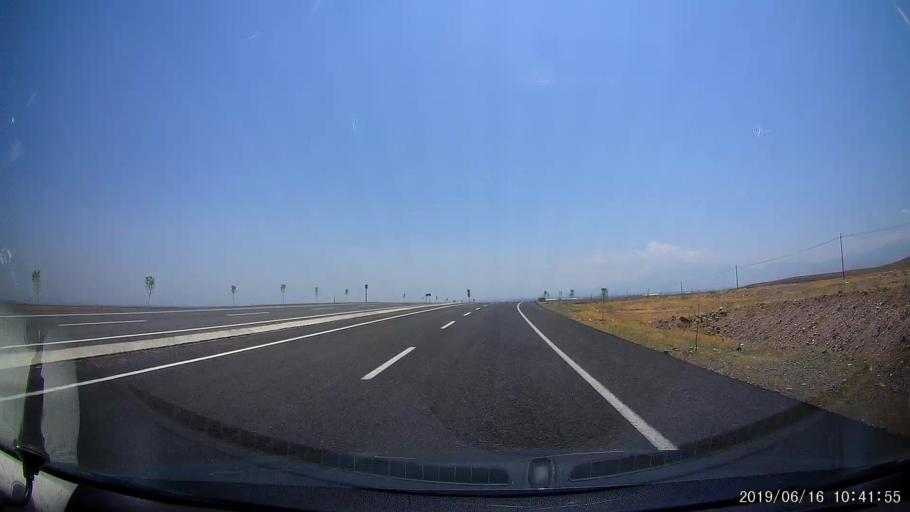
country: AM
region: Armavir
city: Shenavan
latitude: 40.0456
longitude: 43.7953
